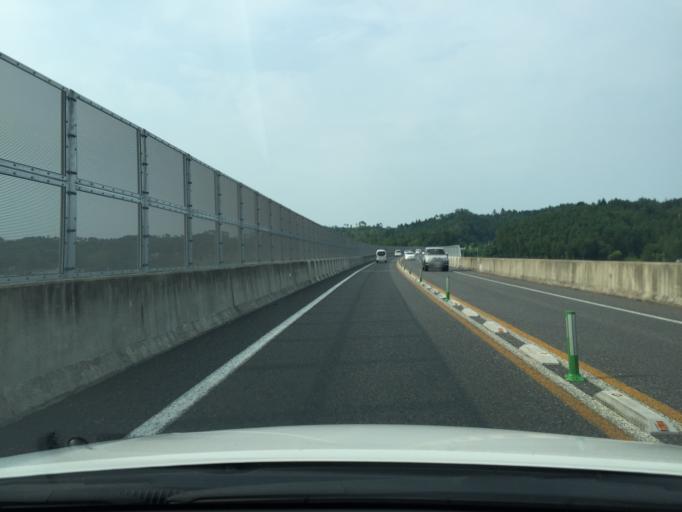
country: JP
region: Fukushima
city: Iwaki
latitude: 37.1665
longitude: 140.9670
